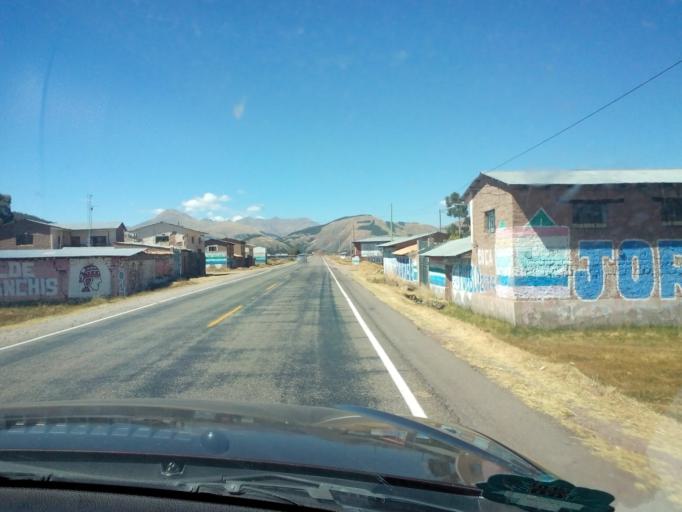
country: PE
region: Cusco
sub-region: Provincia de Canchis
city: San Pablo
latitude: -14.2211
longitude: -71.2884
